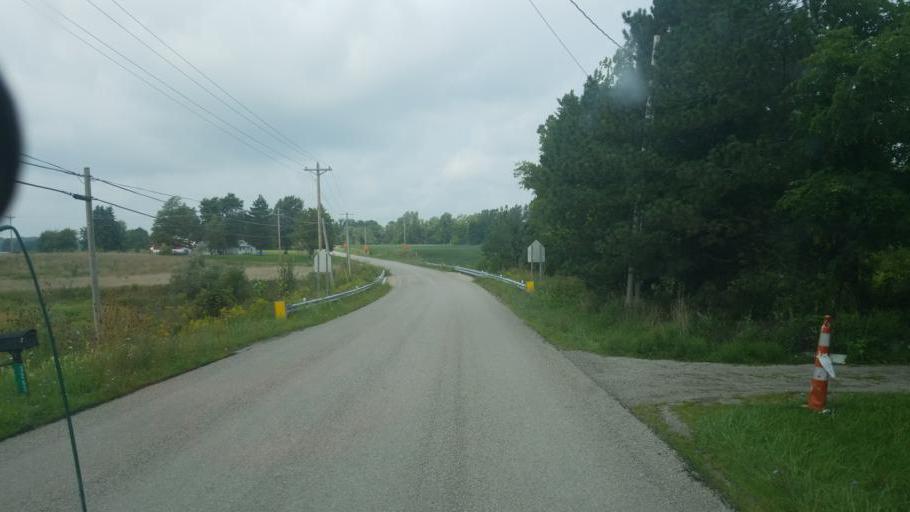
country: US
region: Ohio
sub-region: Huron County
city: Greenwich
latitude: 41.0507
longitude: -82.5192
